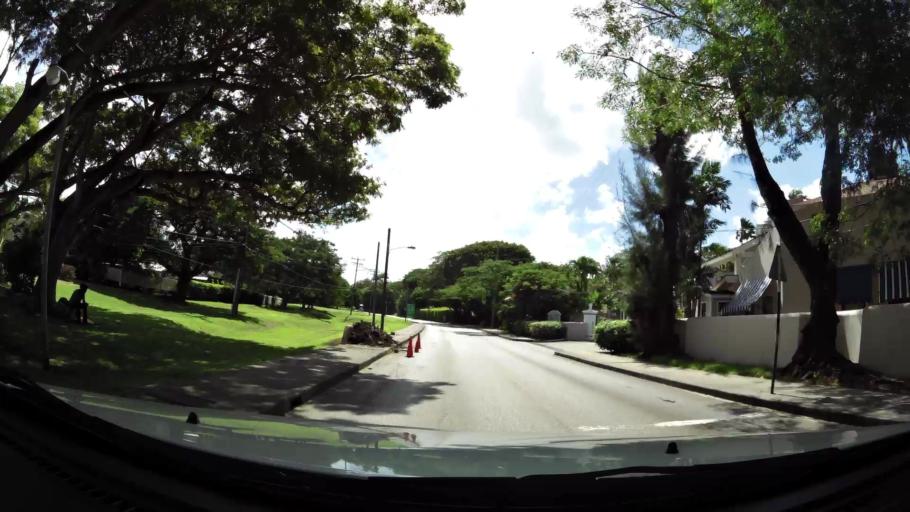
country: BB
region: Saint James
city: Holetown
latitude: 13.1778
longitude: -59.6379
